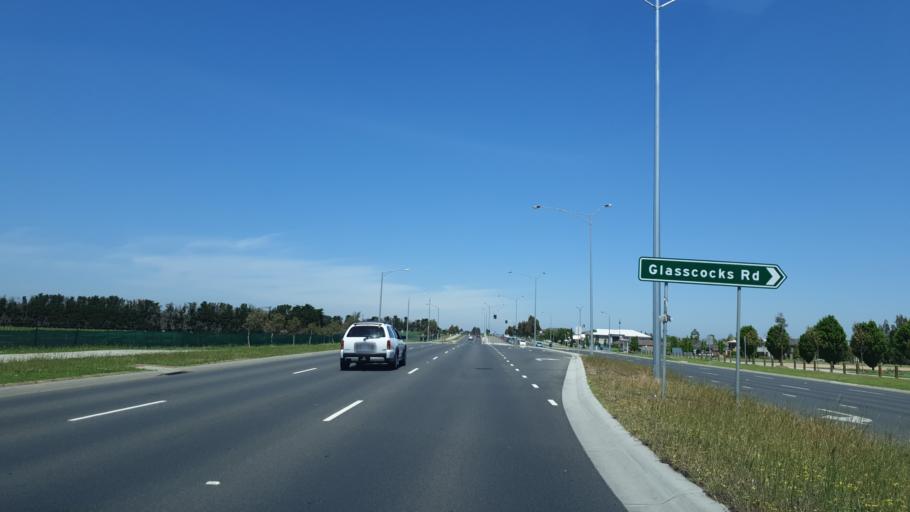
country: AU
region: Victoria
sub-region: Casey
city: Cranbourne North
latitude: -38.0698
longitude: 145.2983
